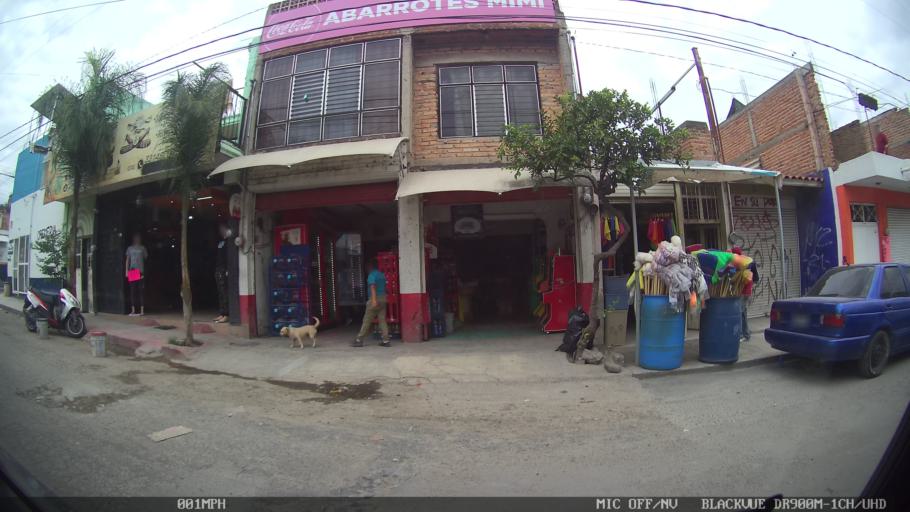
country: MX
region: Jalisco
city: Tlaquepaque
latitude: 20.6535
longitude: -103.2591
